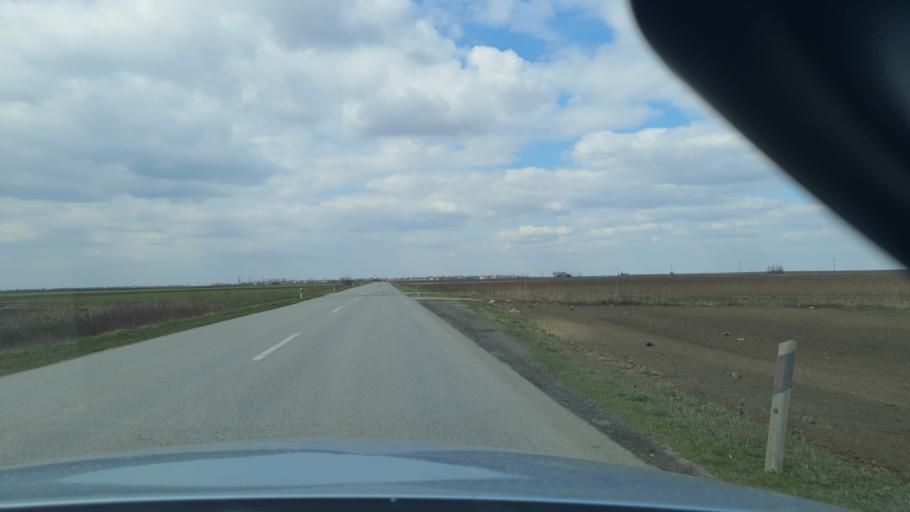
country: RS
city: Maglic
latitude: 45.4015
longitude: 19.4392
